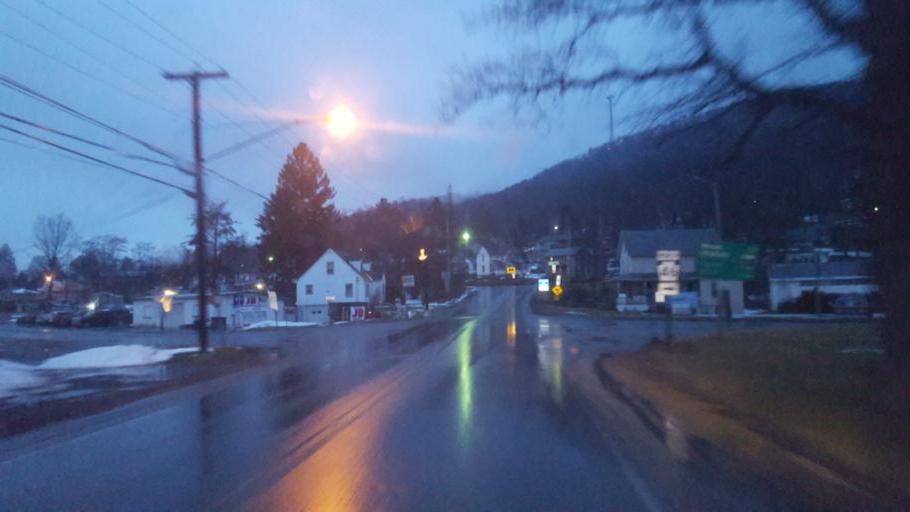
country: US
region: Pennsylvania
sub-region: McKean County
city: Smethport
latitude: 41.8113
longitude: -78.4333
